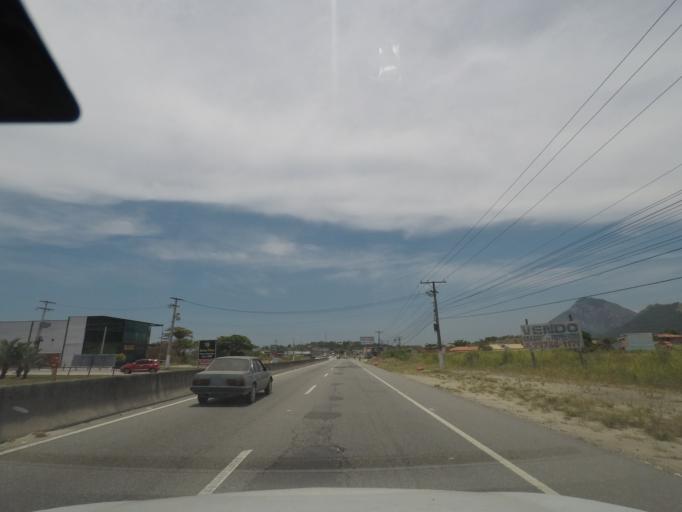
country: BR
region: Rio de Janeiro
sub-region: Marica
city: Marica
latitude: -22.9284
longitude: -42.8696
